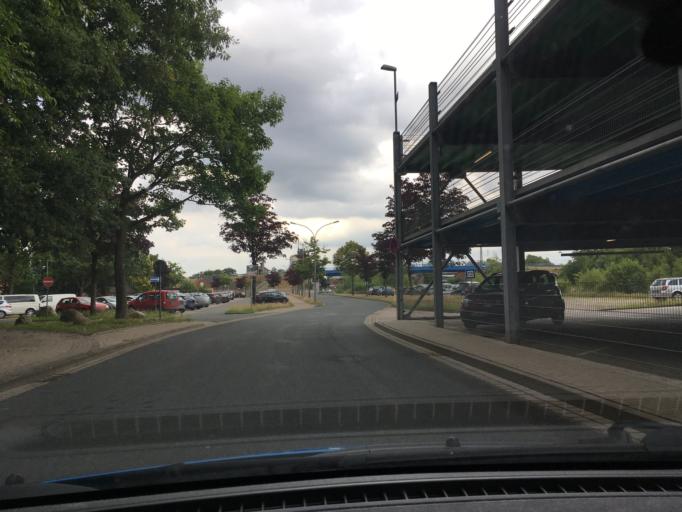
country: DE
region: Lower Saxony
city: Tostedt
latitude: 53.2736
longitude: 9.7343
